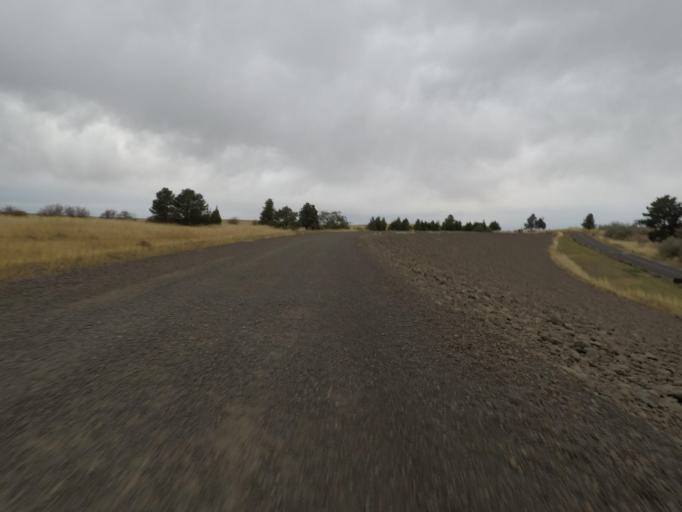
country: US
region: Washington
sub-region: Walla Walla County
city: Walla Walla East
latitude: 46.0653
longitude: -118.2659
